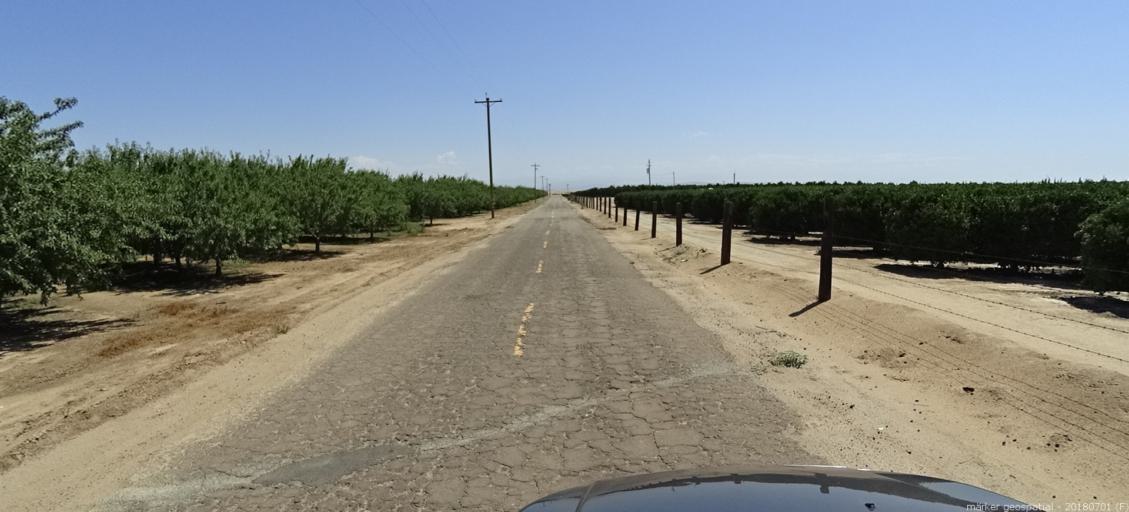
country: US
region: California
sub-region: Madera County
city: Madera Acres
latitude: 37.0776
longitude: -120.0242
